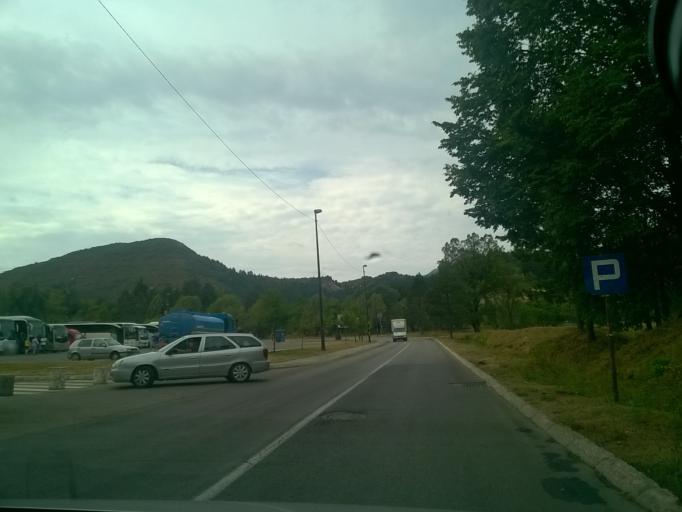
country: ME
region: Cetinje
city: Cetinje
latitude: 42.3861
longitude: 18.9234
